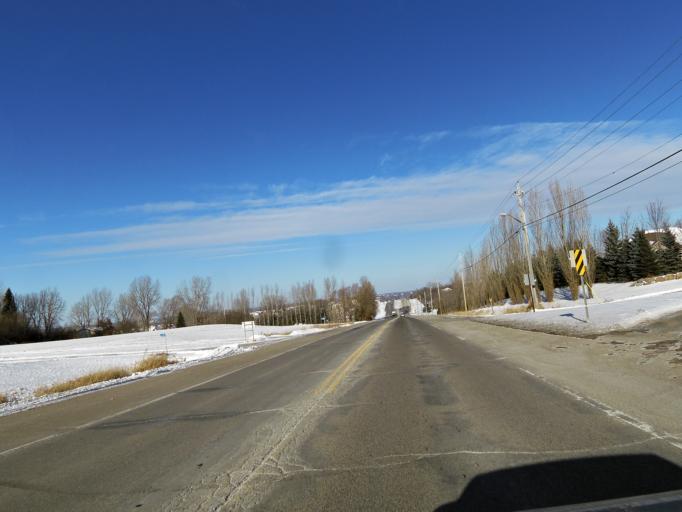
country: US
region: Minnesota
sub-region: Scott County
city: Shakopee
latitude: 44.7543
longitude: -93.5052
